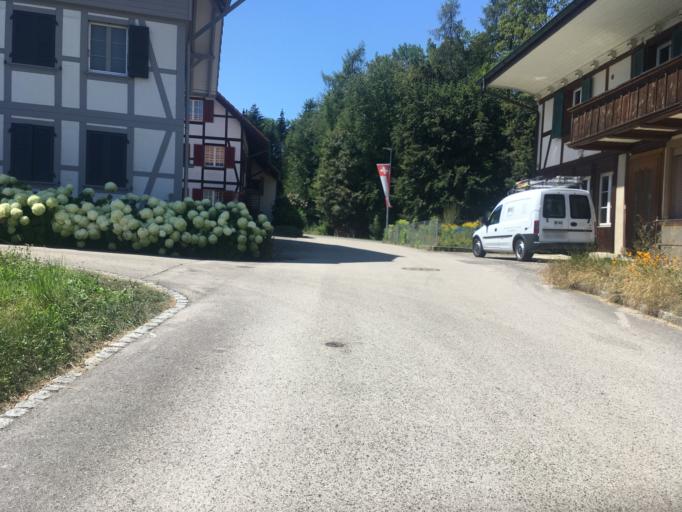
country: CH
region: Solothurn
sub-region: Bezirk Bucheggberg
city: Messen
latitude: 47.0865
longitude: 7.4676
